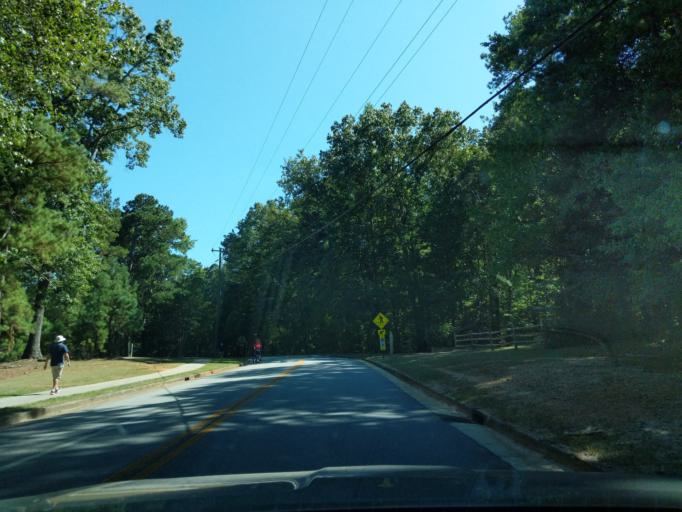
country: US
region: Georgia
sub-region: DeKalb County
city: Stone Mountain
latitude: 33.8077
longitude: -84.1644
